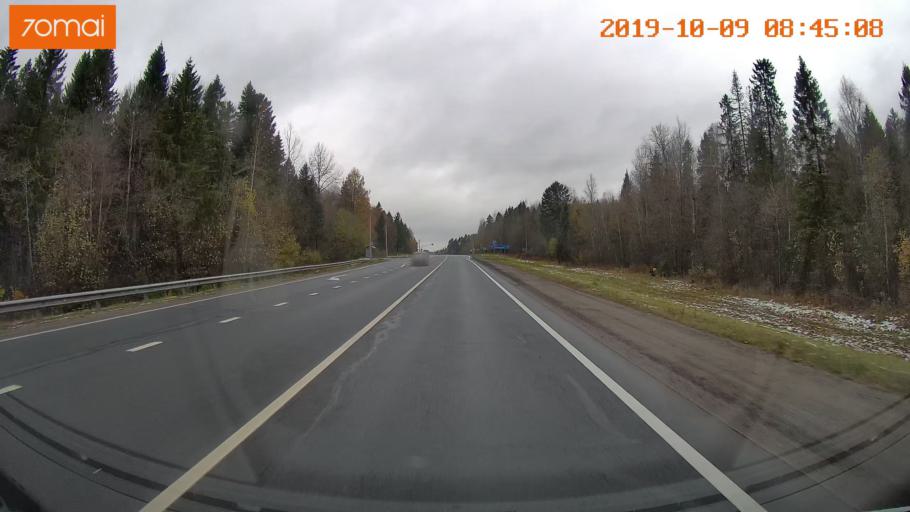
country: RU
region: Vologda
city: Gryazovets
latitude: 59.0450
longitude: 40.0972
